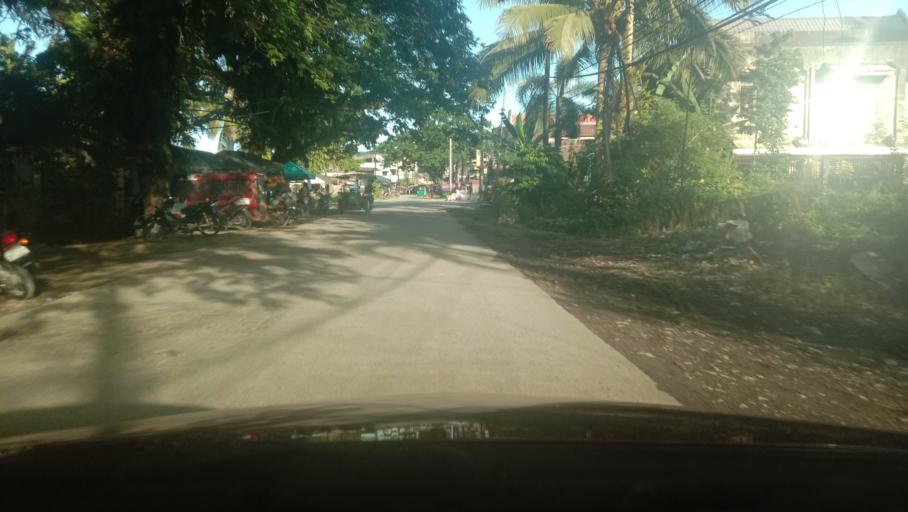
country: PH
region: Caraga
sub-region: Province of Agusan del Sur
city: San Francisco
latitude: 8.5099
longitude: 125.9750
